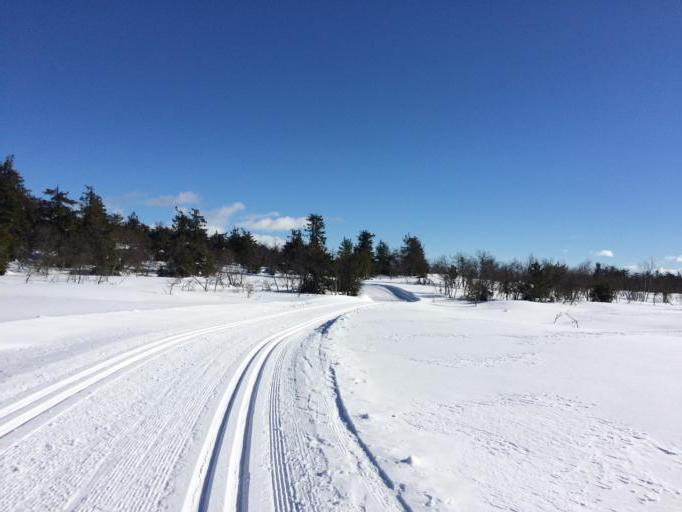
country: NO
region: Oppland
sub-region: Gausdal
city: Segalstad bru
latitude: 61.3085
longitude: 10.1011
